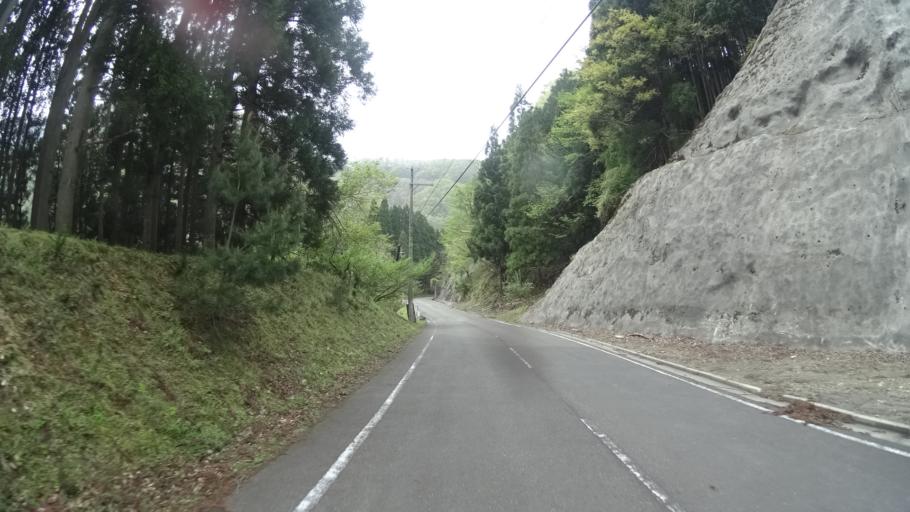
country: JP
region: Kyoto
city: Maizuru
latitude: 35.3569
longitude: 135.4692
